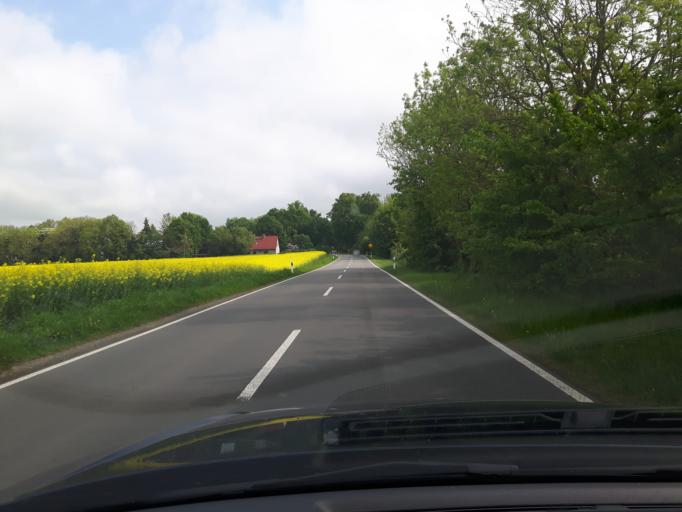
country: DE
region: Mecklenburg-Vorpommern
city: Gross Wokern
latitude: 53.6387
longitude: 12.4830
